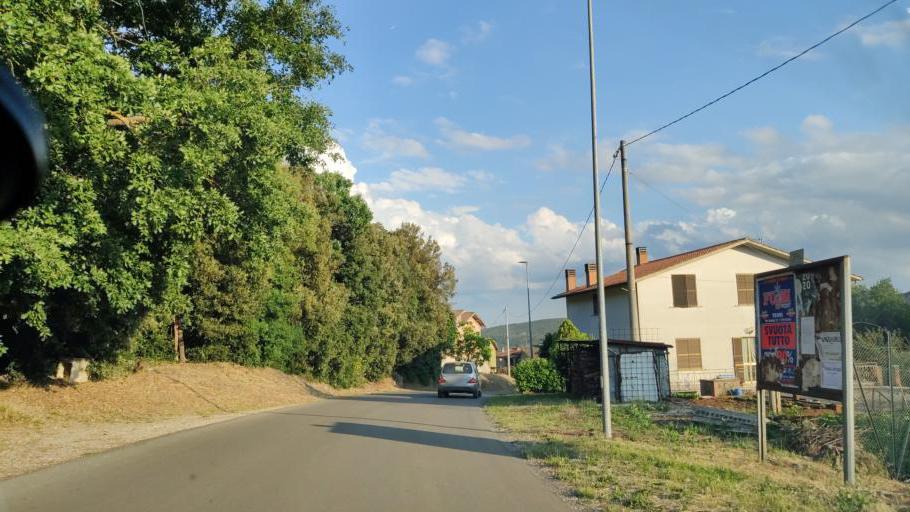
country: IT
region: Umbria
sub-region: Provincia di Terni
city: Lugnano in Teverina
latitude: 42.5970
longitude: 12.3672
